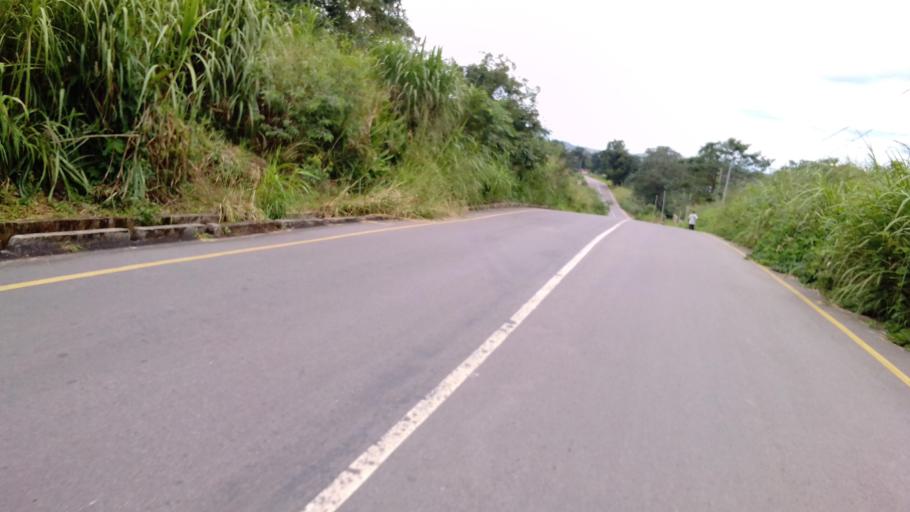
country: SL
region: Eastern Province
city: Koidu
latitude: 8.6515
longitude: -10.9843
